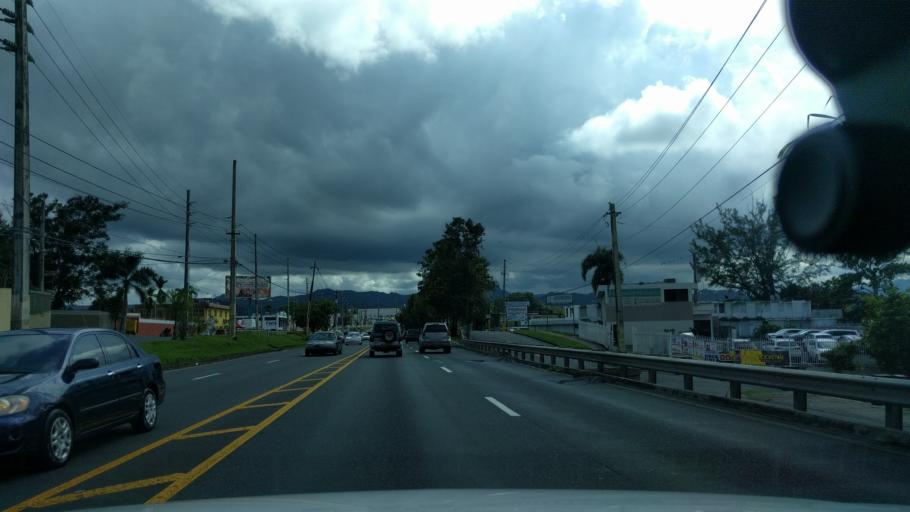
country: PR
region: Toa Alta
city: Pajaros
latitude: 18.3539
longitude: -66.1892
